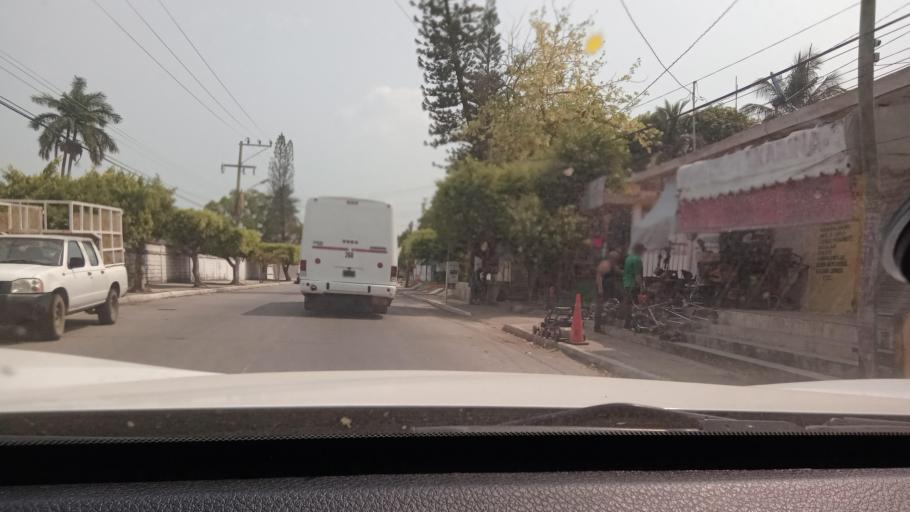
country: MX
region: Veracruz
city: Minatitlan
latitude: 17.9846
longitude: -94.5691
